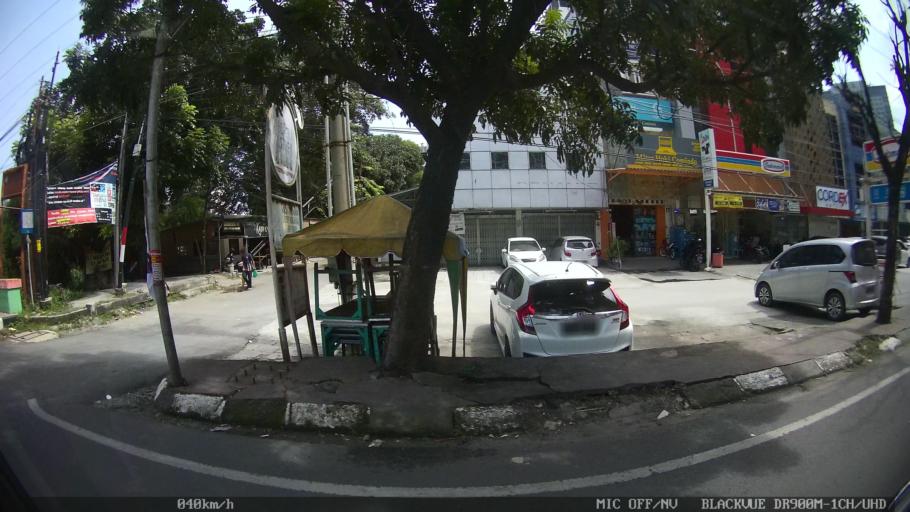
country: ID
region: North Sumatra
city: Medan
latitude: 3.5948
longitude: 98.6730
